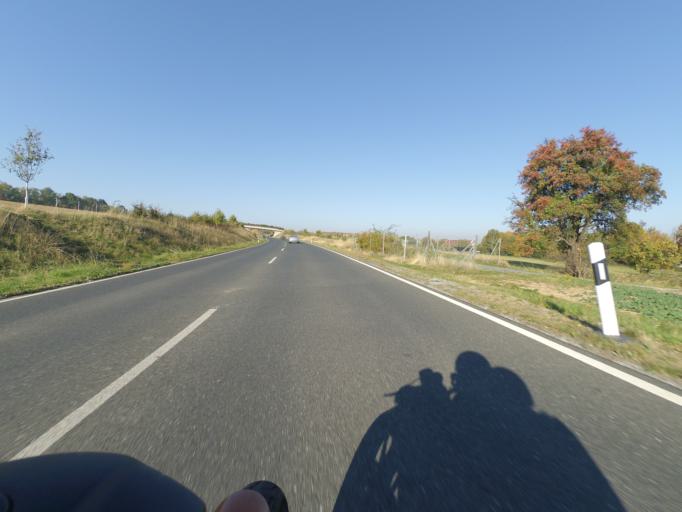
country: DE
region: Saxony
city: Bannewitz
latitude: 50.9892
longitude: 13.7229
